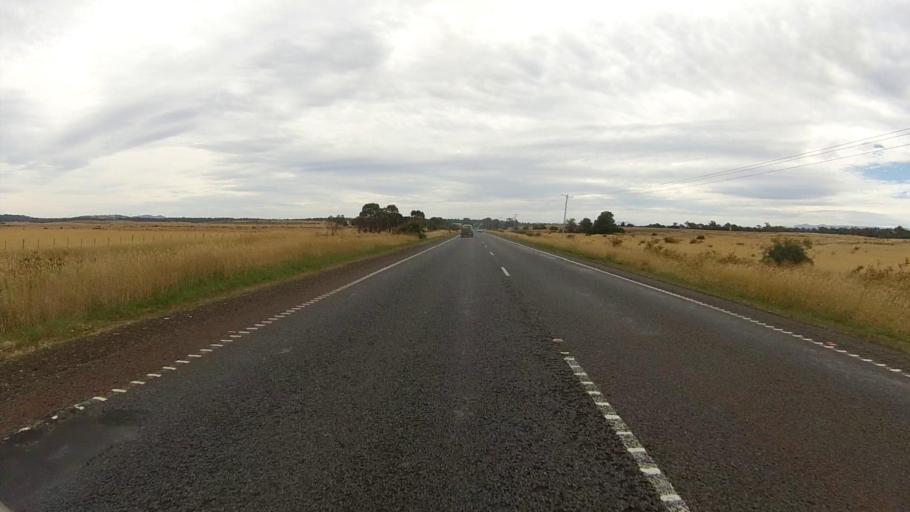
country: AU
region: Tasmania
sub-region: Northern Midlands
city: Evandale
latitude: -41.8578
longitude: 147.4543
